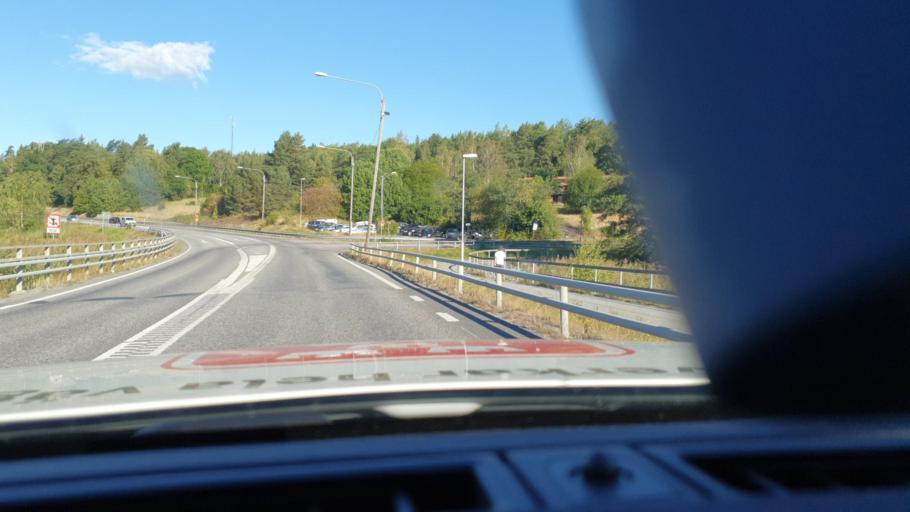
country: SE
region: Stockholm
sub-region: Vaxholms Kommun
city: Resaro
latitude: 59.4168
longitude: 18.3108
